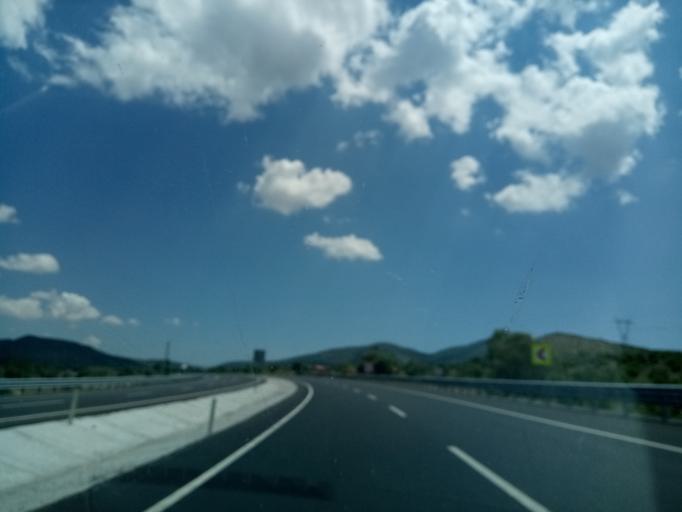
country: TR
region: Konya
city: Cavus
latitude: 37.6619
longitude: 31.9896
